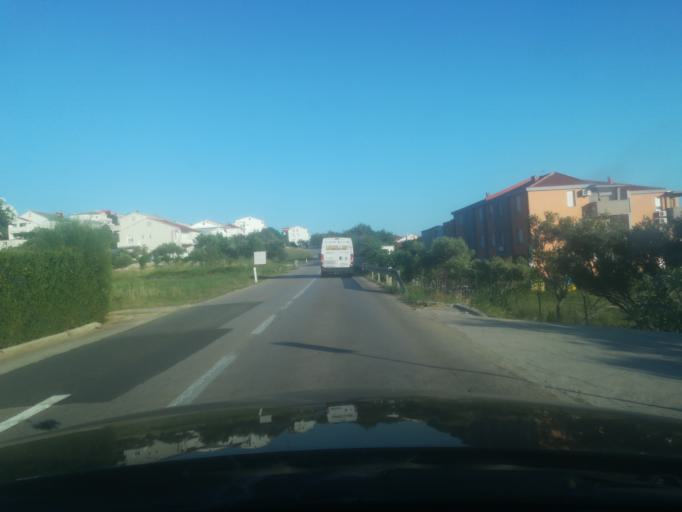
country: HR
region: Primorsko-Goranska
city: Banjol
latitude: 44.7473
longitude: 14.7893
